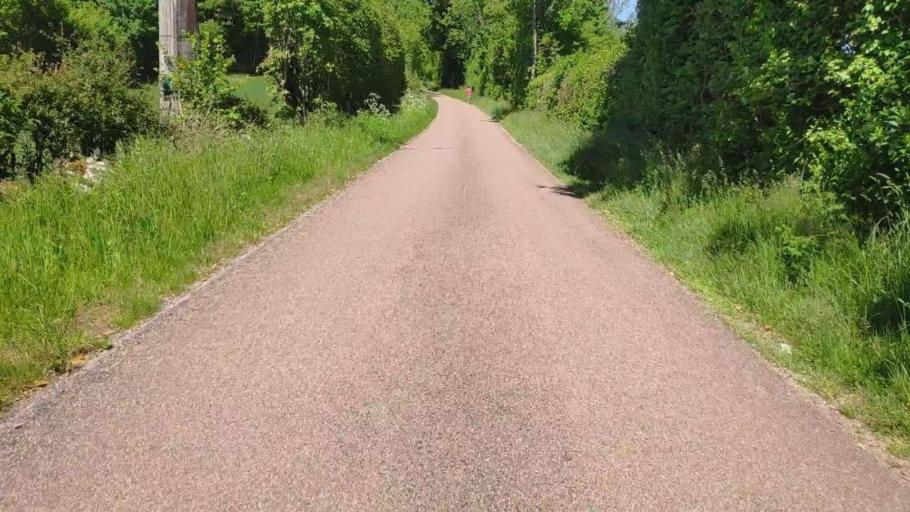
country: FR
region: Franche-Comte
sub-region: Departement du Jura
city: Poligny
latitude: 46.7310
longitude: 5.7396
